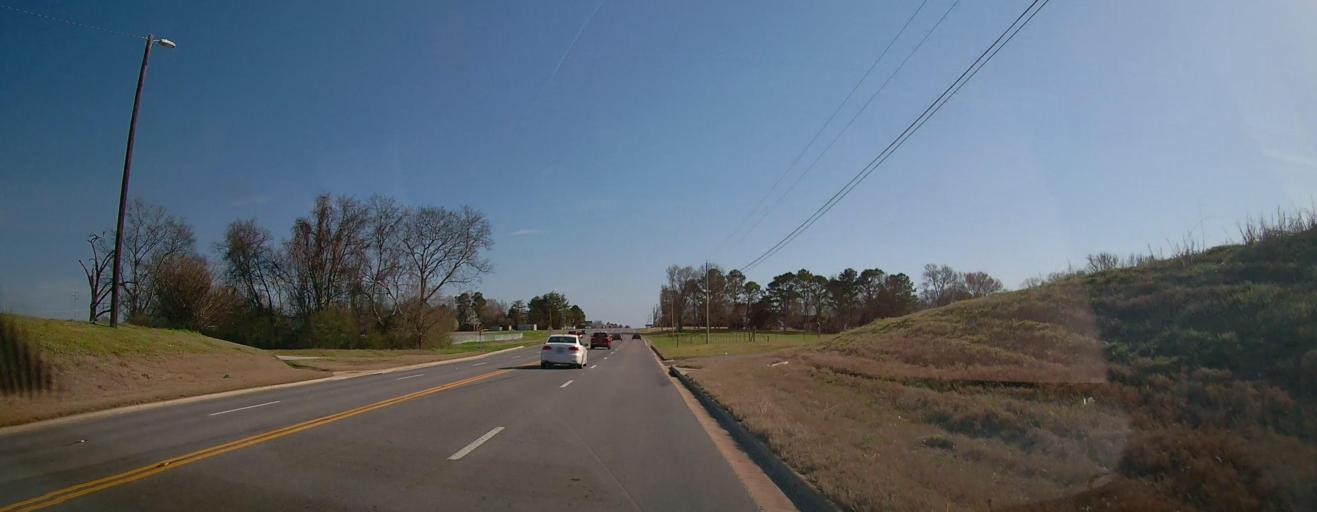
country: US
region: Alabama
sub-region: Colbert County
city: Muscle Shoals
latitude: 34.7135
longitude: -87.6350
